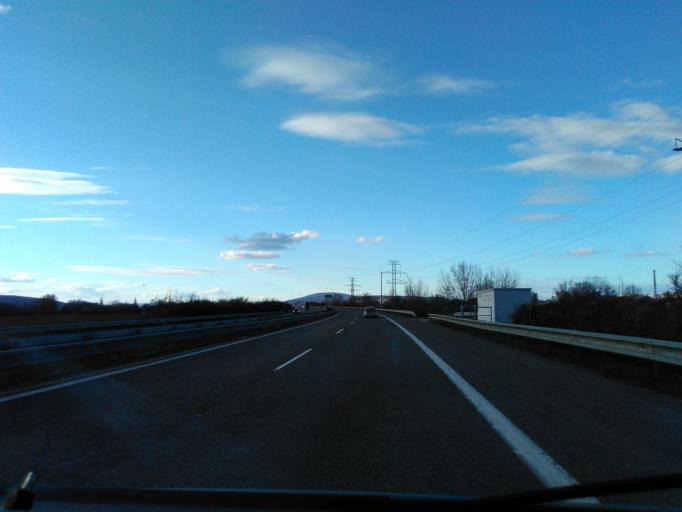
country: AT
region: Burgenland
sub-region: Politischer Bezirk Neusiedl am See
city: Kittsee
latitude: 48.1018
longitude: 17.0955
